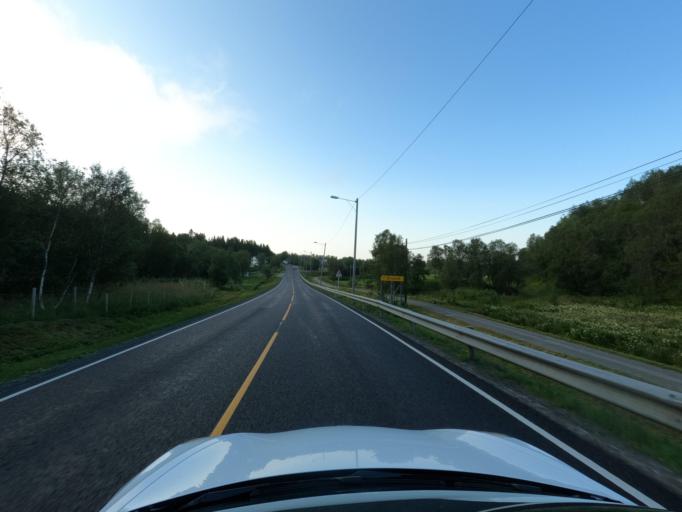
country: NO
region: Troms
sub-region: Skanland
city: Evenskjer
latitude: 68.6666
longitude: 16.5758
